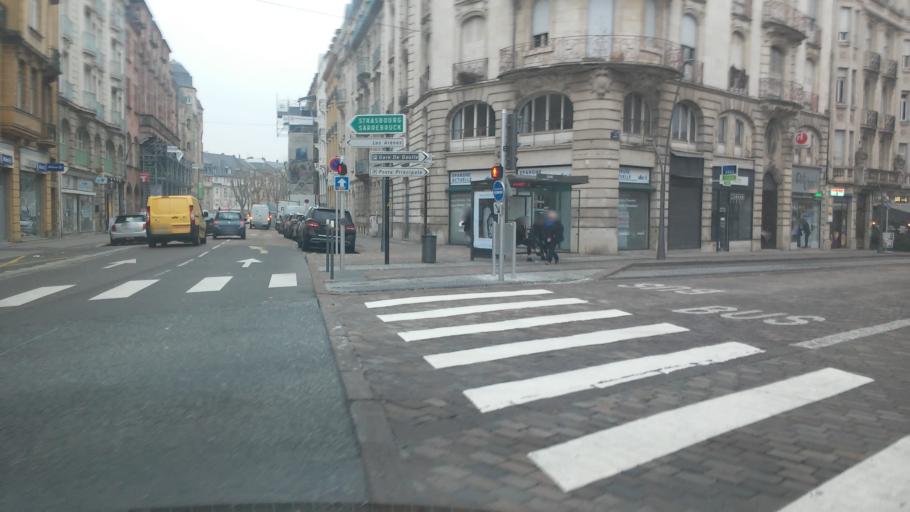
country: FR
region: Lorraine
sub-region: Departement de la Moselle
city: Metz
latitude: 49.1103
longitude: 6.1748
